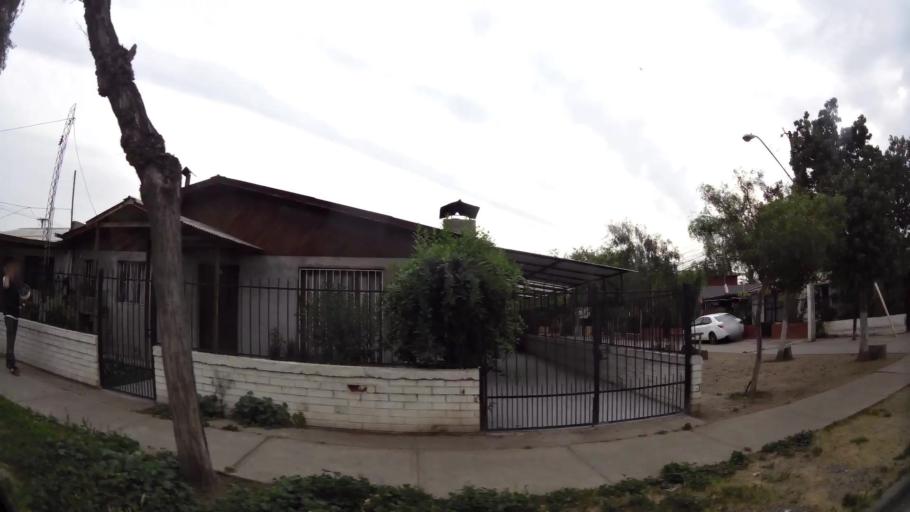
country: CL
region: Santiago Metropolitan
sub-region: Provincia de Santiago
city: Lo Prado
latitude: -33.4959
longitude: -70.7624
